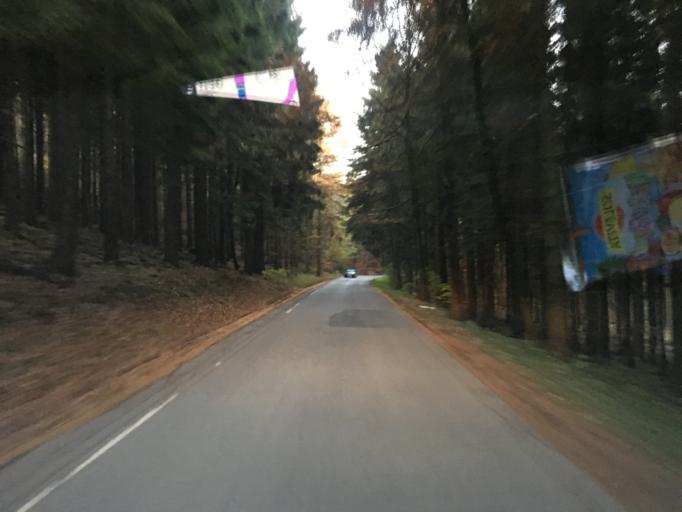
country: DE
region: North Rhine-Westphalia
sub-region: Regierungsbezirk Arnsberg
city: Nachrodt-Wiblingwerde
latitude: 51.2680
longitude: 7.6084
